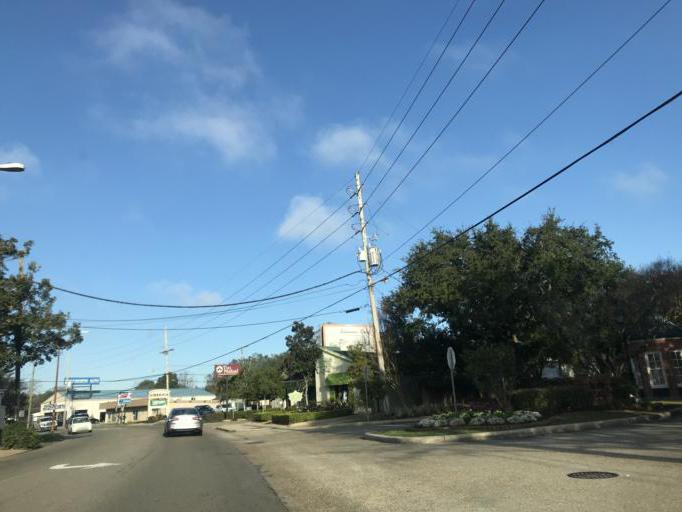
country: US
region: Louisiana
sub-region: Jefferson Parish
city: Metairie
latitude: 29.9885
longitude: -90.1317
